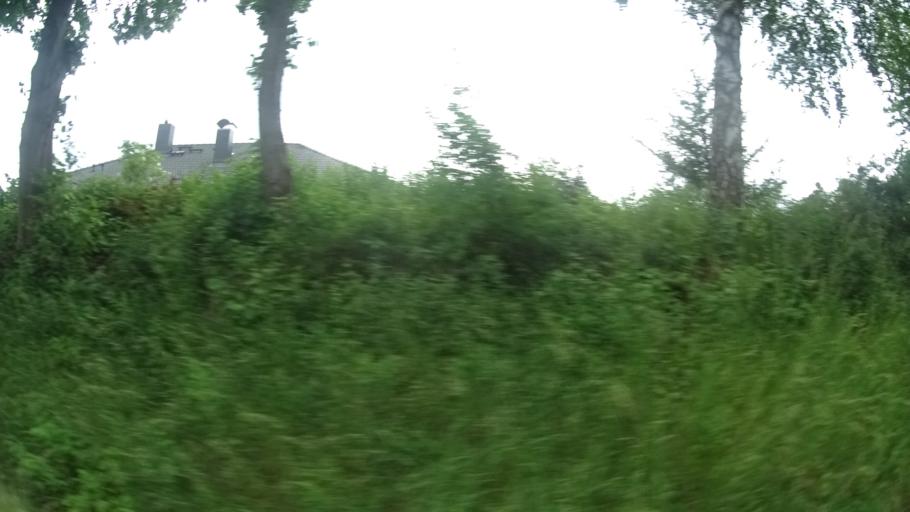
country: DE
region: Hesse
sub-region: Regierungsbezirk Kassel
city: Fulda
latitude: 50.5255
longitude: 9.6590
